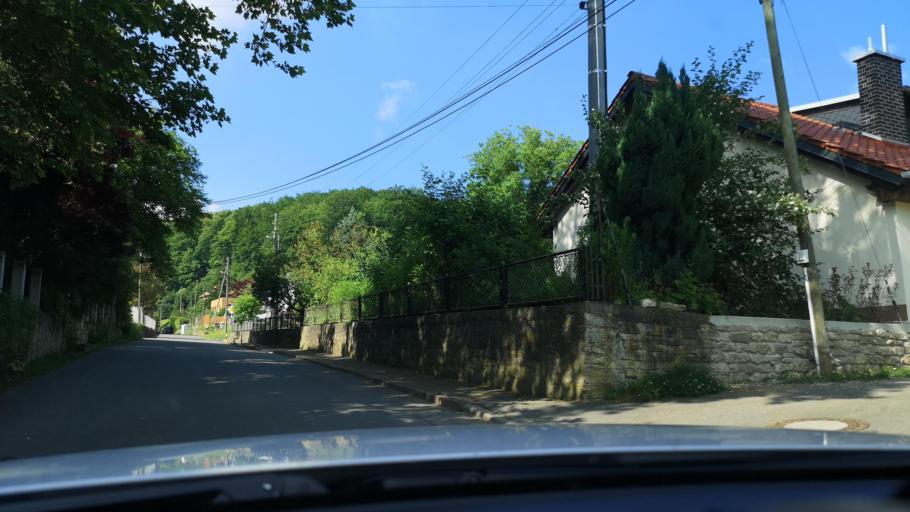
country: DE
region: Thuringia
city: Tautenburg
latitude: 50.9901
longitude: 11.7132
